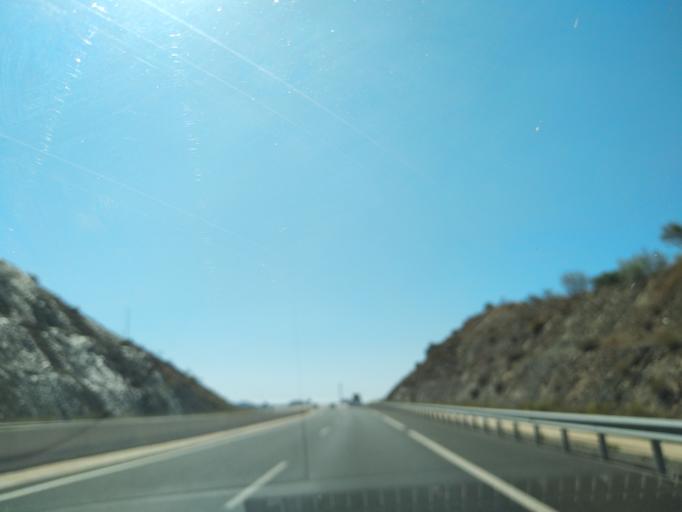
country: ES
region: Andalusia
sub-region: Provincia de Malaga
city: Almogia
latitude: 36.8443
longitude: -4.4840
